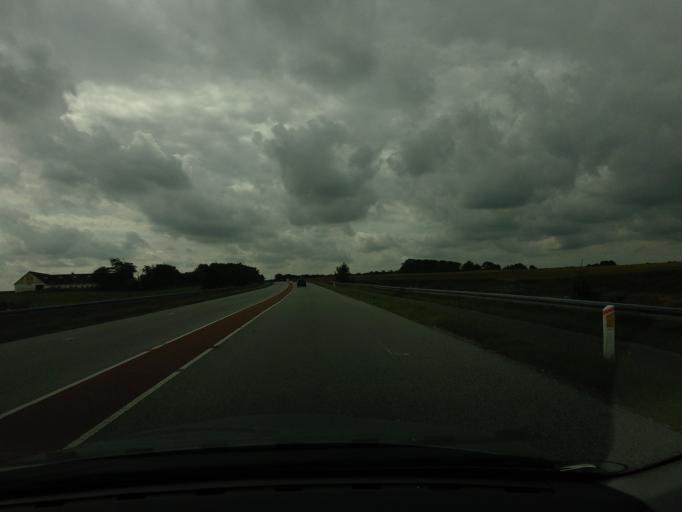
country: DK
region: North Denmark
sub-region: Hjorring Kommune
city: Hjorring
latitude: 57.4203
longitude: 9.9914
